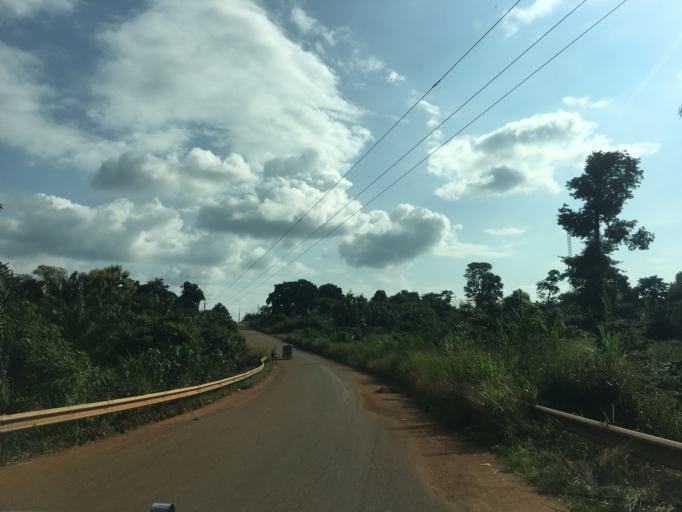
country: GH
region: Western
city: Bibiani
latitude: 6.8006
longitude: -2.5226
